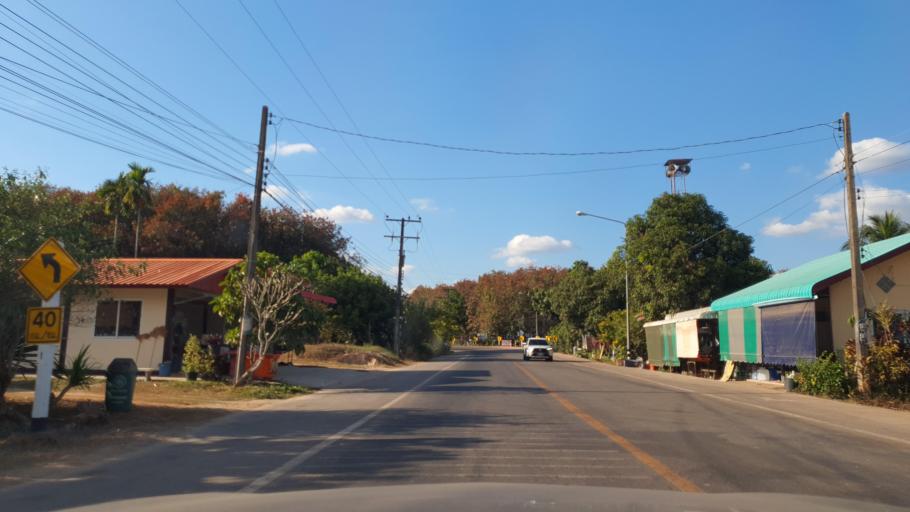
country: TH
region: Nong Khai
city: Bueng Khong Long
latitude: 18.0105
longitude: 104.0077
